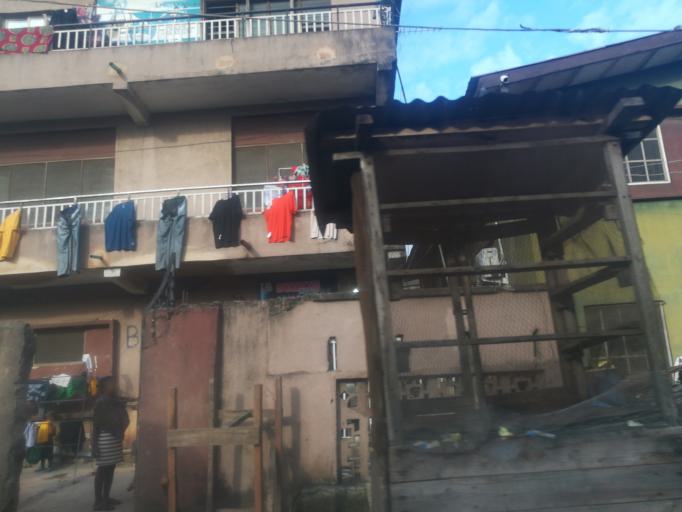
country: NG
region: Lagos
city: Somolu
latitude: 6.5429
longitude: 3.3882
